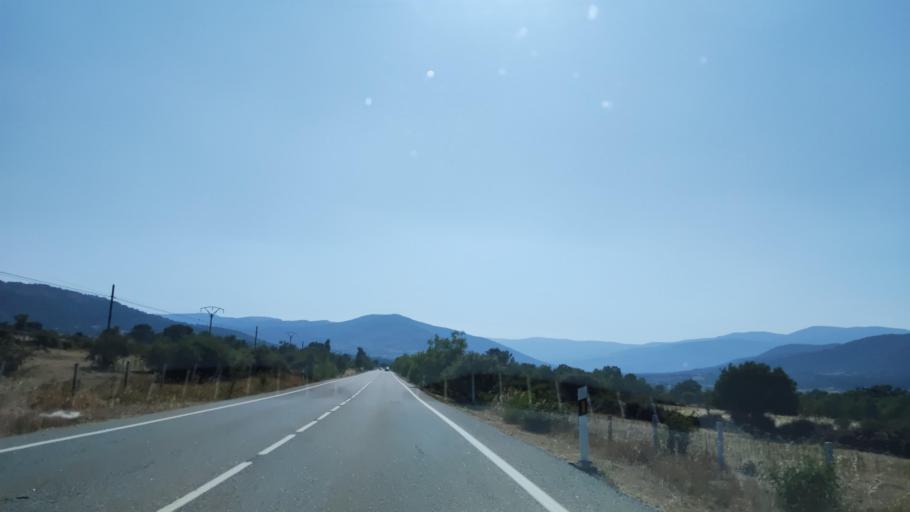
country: ES
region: Madrid
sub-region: Provincia de Madrid
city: Garganta de los Montes
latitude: 40.9440
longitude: -3.6883
